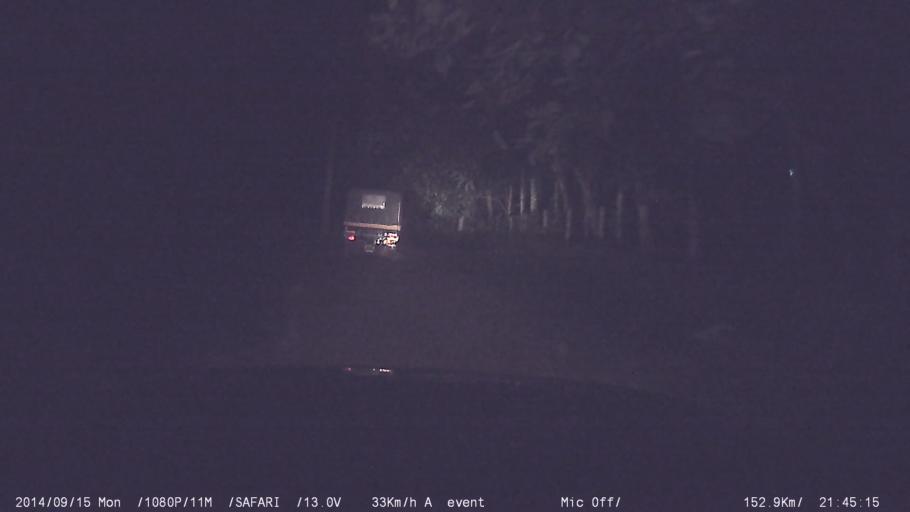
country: IN
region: Kerala
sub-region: Kottayam
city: Palackattumala
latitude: 9.7738
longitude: 76.5595
